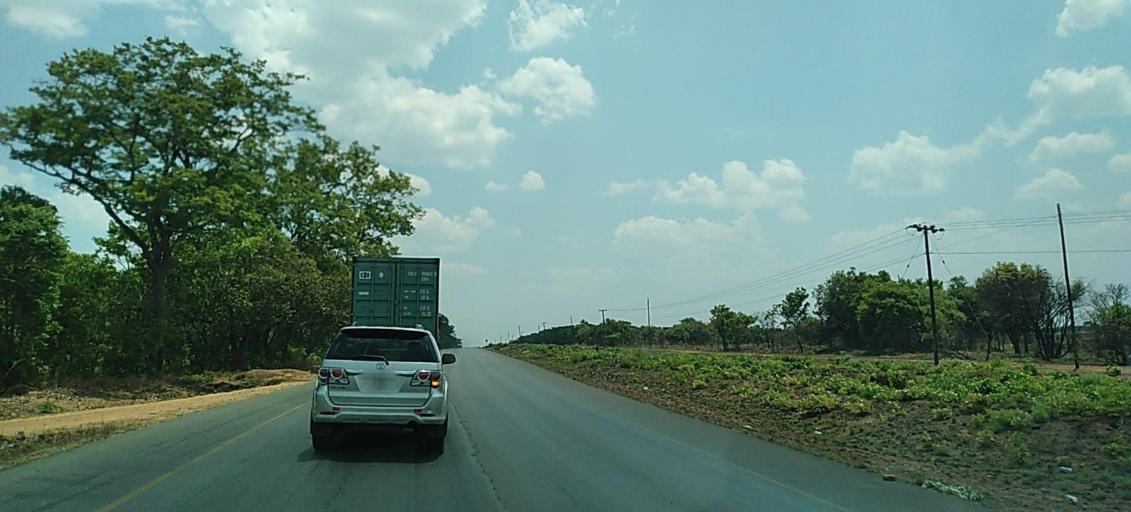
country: ZM
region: Central
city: Kabwe
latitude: -14.3207
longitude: 28.5456
